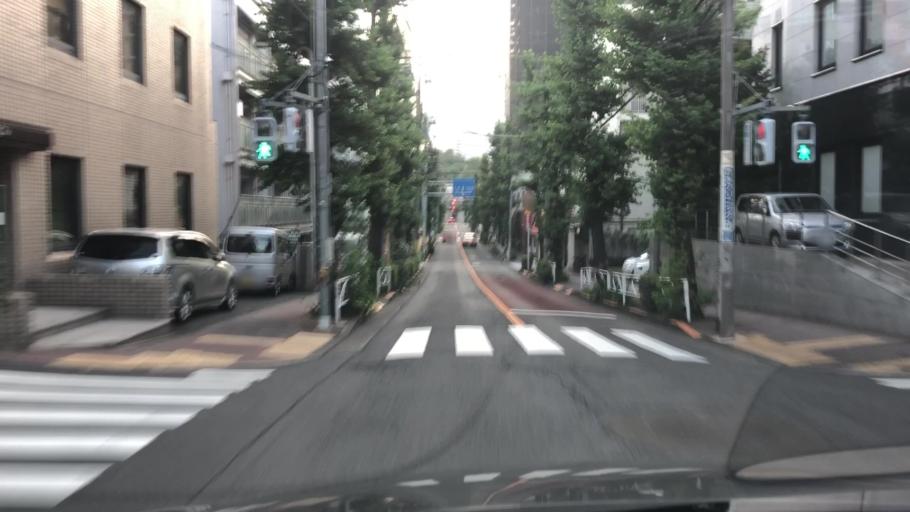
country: JP
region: Tokyo
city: Tokyo
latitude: 35.6469
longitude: 139.6930
